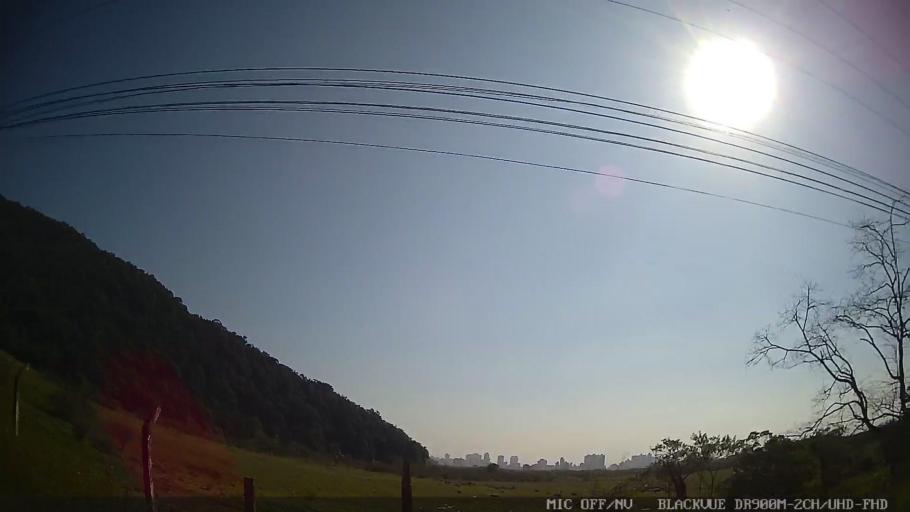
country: BR
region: Sao Paulo
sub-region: Guaruja
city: Guaruja
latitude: -24.0121
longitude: -46.3011
